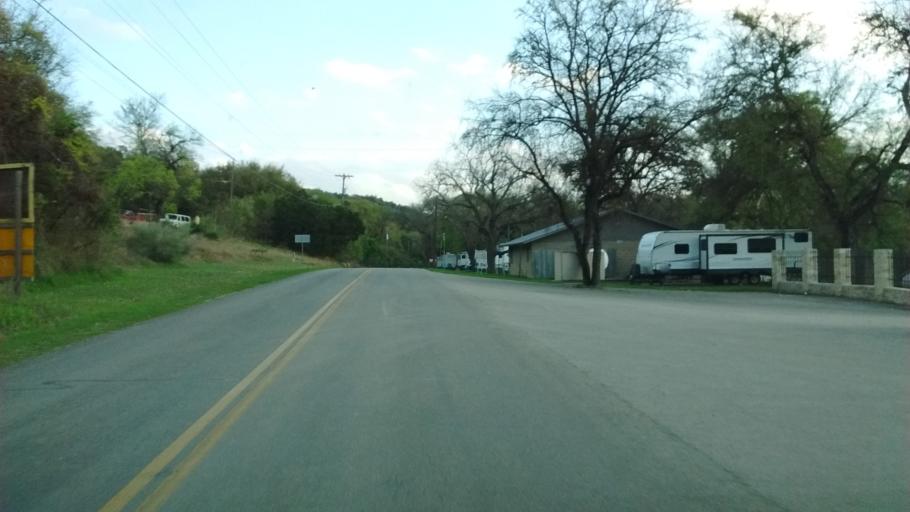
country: US
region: Texas
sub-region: Comal County
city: New Braunfels
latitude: 29.7757
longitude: -98.1593
